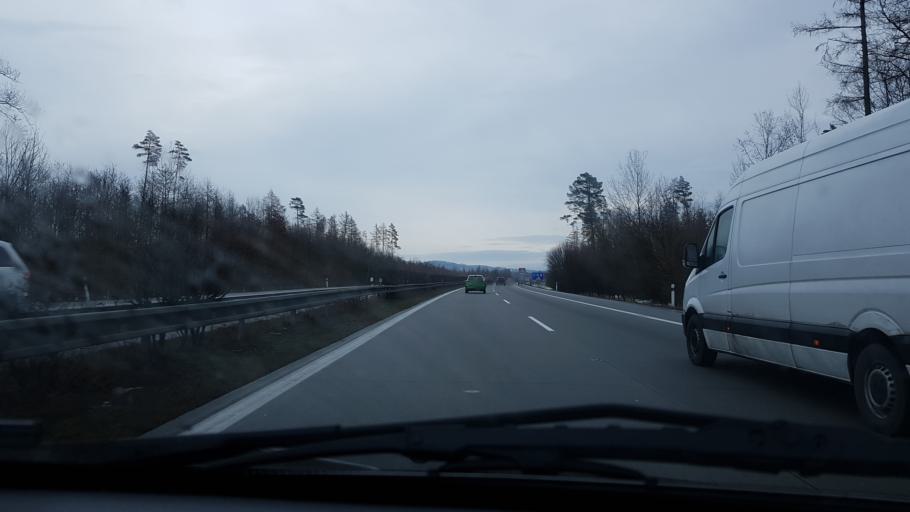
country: CZ
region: Olomoucky
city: Velky Ujezd
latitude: 49.5823
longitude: 17.4548
